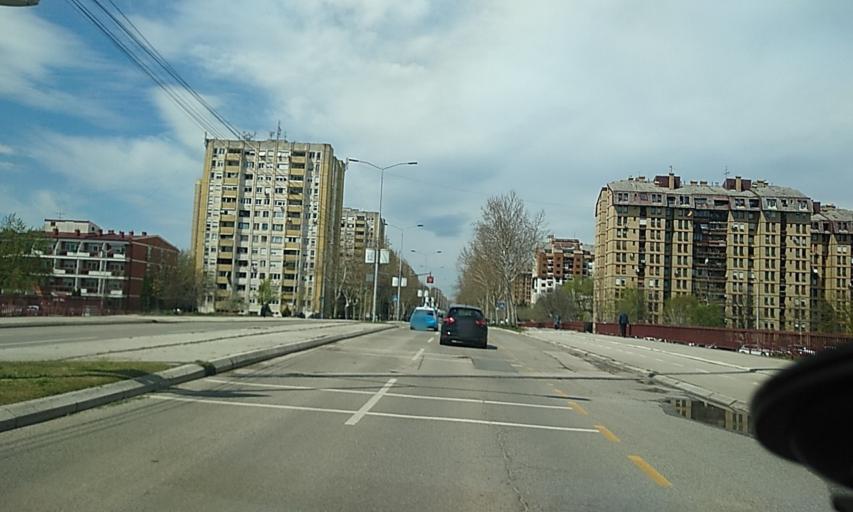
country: RS
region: Central Serbia
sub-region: Nisavski Okrug
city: Nis
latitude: 43.3162
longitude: 21.9263
